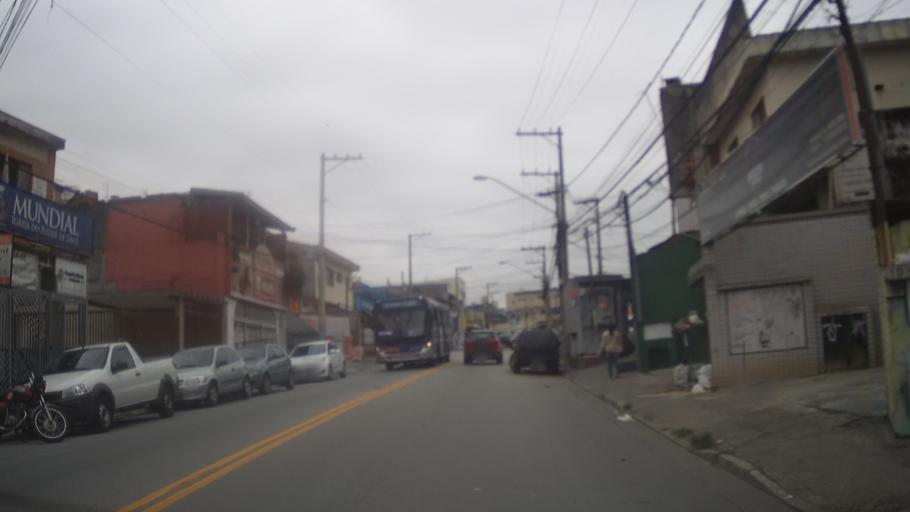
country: BR
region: Sao Paulo
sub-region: Guarulhos
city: Guarulhos
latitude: -23.4415
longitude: -46.5486
